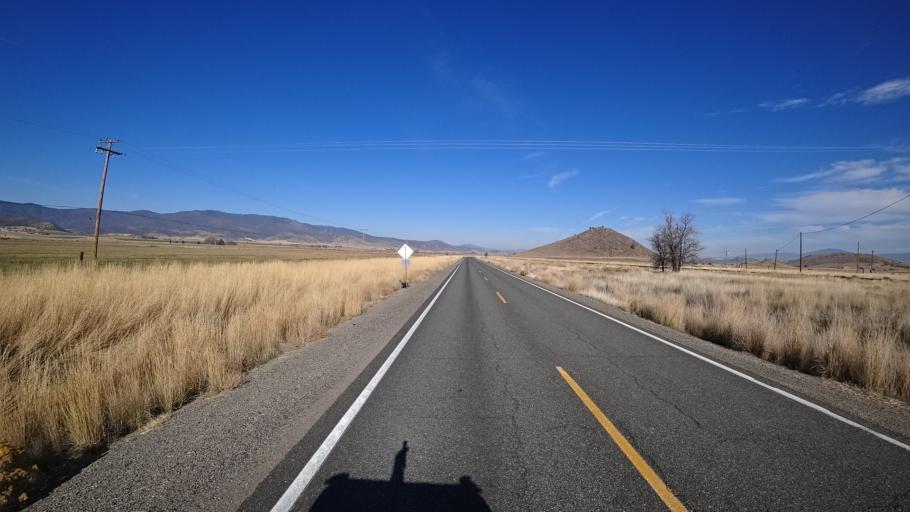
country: US
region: California
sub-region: Siskiyou County
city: Weed
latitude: 41.5268
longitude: -122.5221
